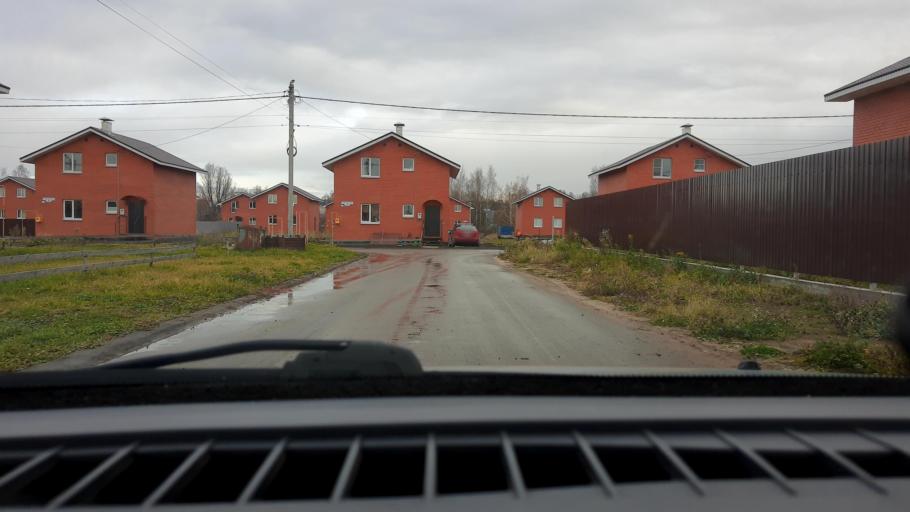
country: RU
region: Nizjnij Novgorod
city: Afonino
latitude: 56.2068
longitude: 44.1213
